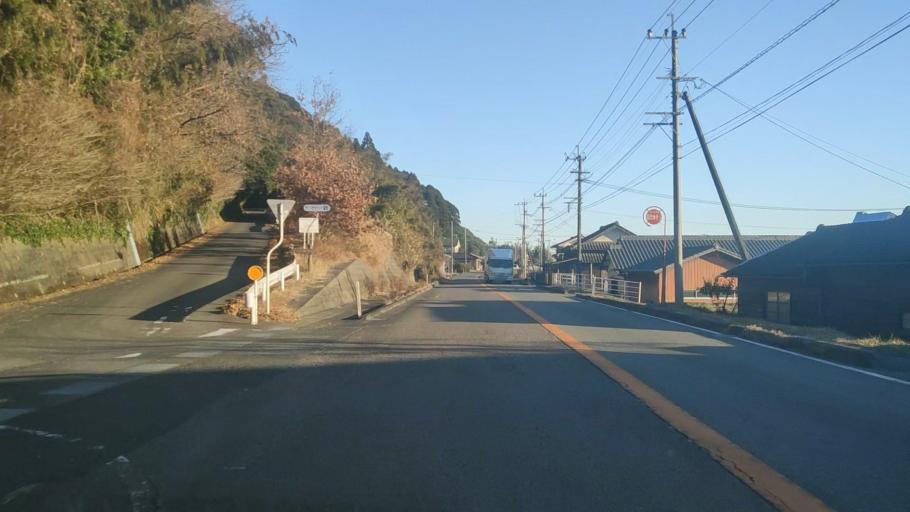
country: JP
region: Miyazaki
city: Takanabe
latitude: 32.0829
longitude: 131.5102
